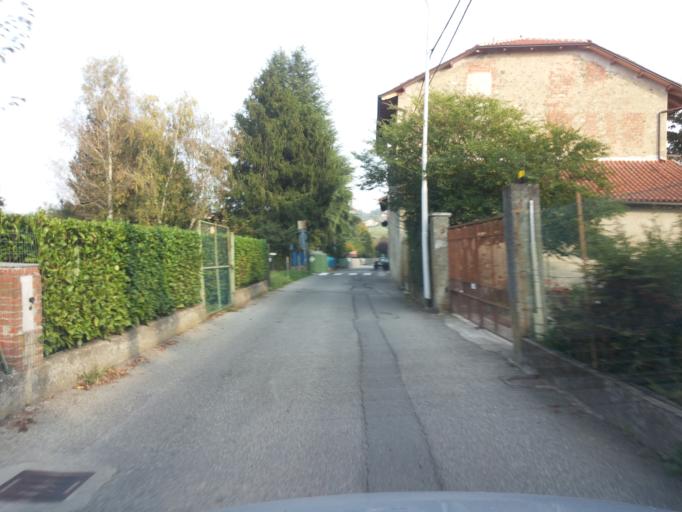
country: IT
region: Piedmont
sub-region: Provincia di Biella
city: Viverone
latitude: 45.4016
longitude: 8.0448
